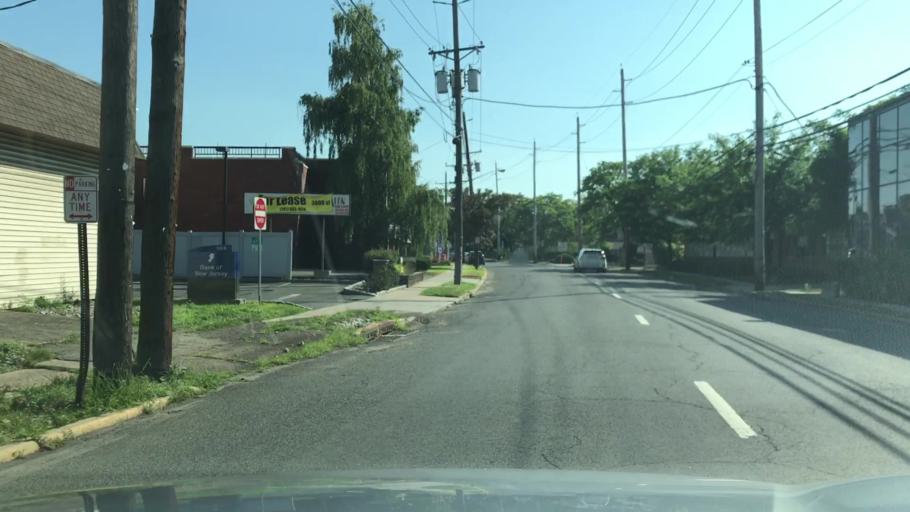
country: US
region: New Jersey
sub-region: Bergen County
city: Englewood
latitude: 40.8907
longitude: -73.9763
